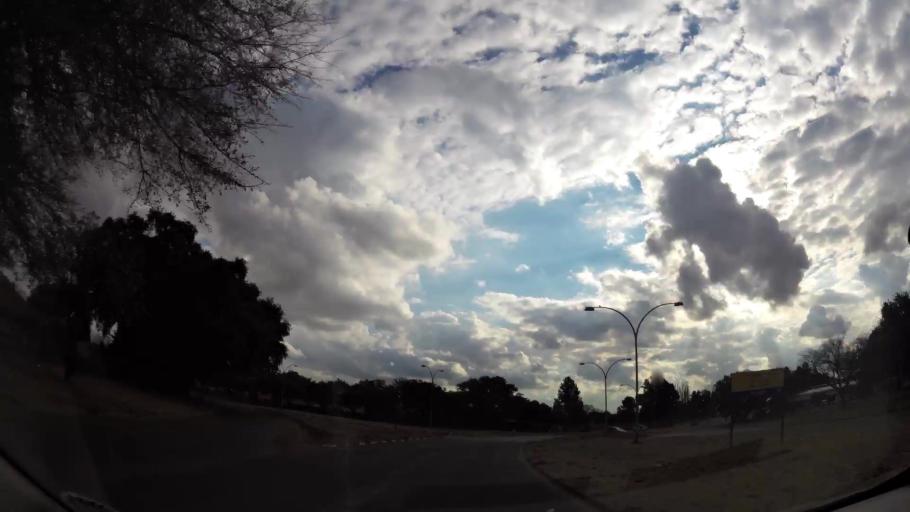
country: ZA
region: Orange Free State
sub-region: Fezile Dabi District Municipality
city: Sasolburg
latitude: -26.8041
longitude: 27.8132
